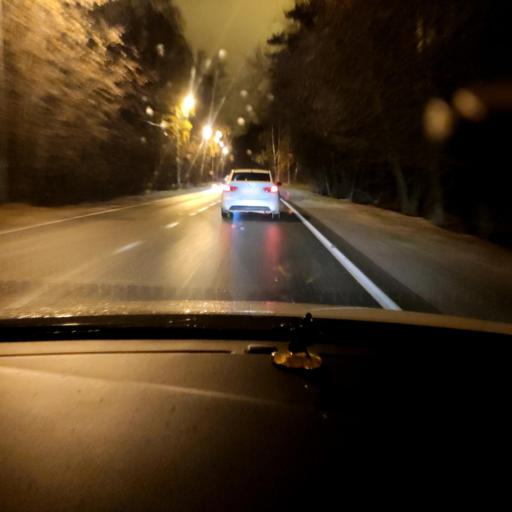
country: RU
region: Tatarstan
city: Osinovo
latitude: 55.8314
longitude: 48.8926
